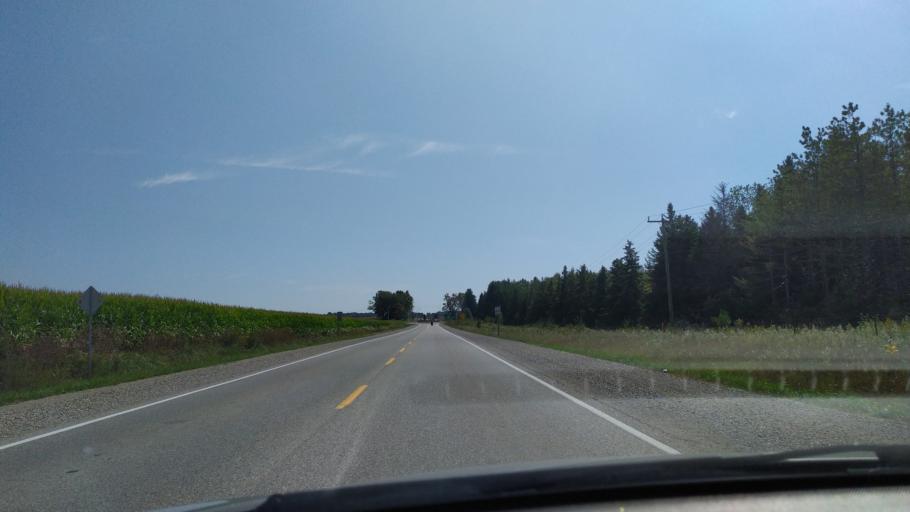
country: CA
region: Ontario
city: Ingersoll
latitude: 43.1009
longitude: -80.8742
